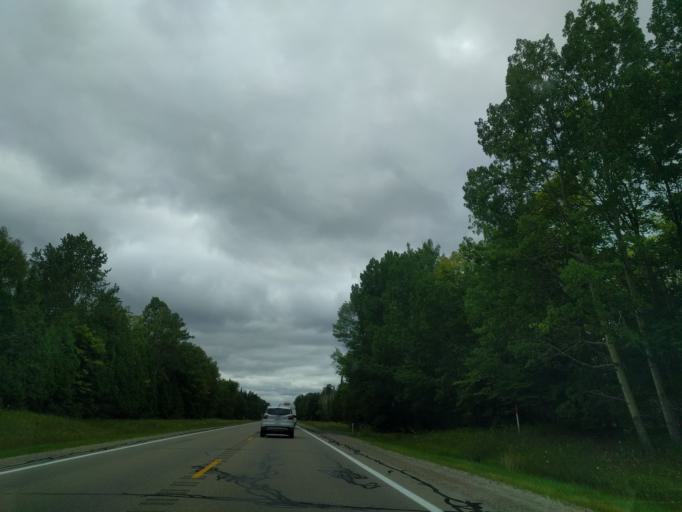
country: US
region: Michigan
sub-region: Menominee County
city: Menominee
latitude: 45.3428
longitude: -87.4127
